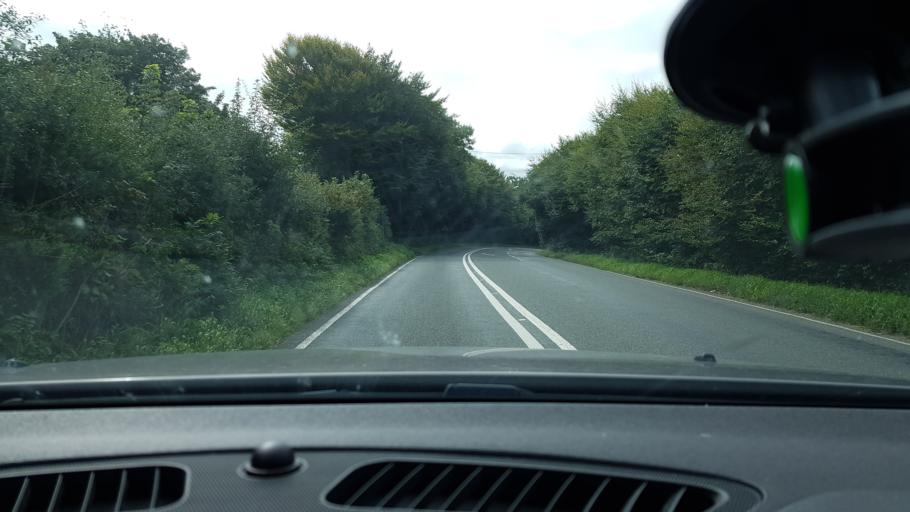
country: GB
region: England
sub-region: Cornwall
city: Camelford
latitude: 50.5960
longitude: -4.7163
